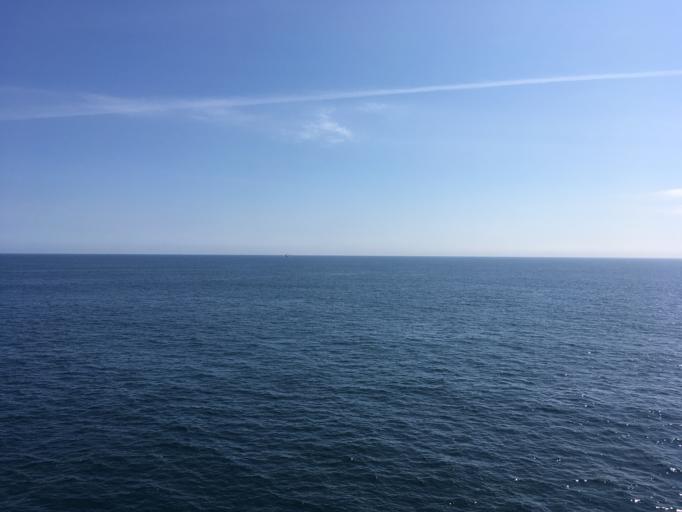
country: IE
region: Leinster
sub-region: Loch Garman
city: Ballygerry
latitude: 52.1793
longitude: -5.8613
